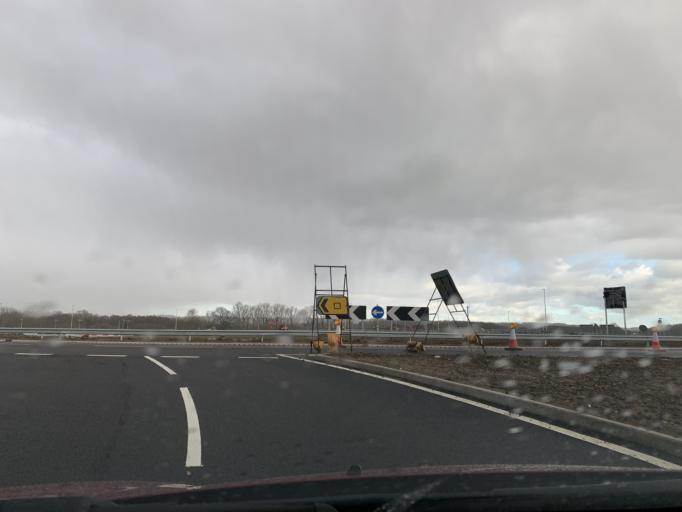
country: GB
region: England
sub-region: Kent
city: Ashford
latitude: 51.1324
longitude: 0.9196
